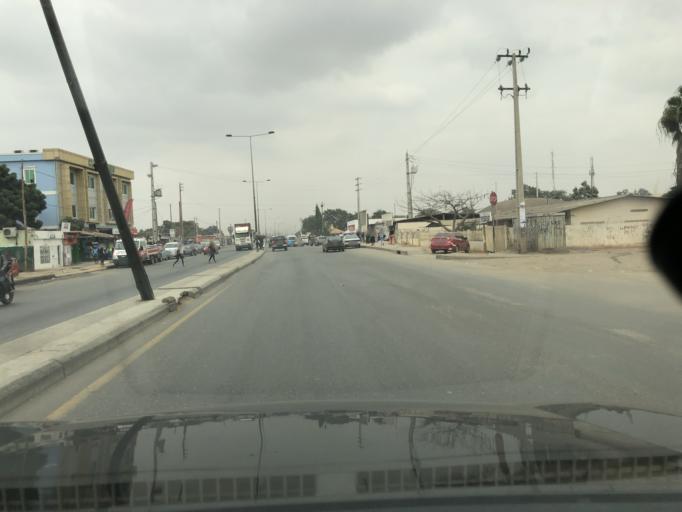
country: AO
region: Luanda
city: Luanda
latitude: -8.8270
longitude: 13.2825
